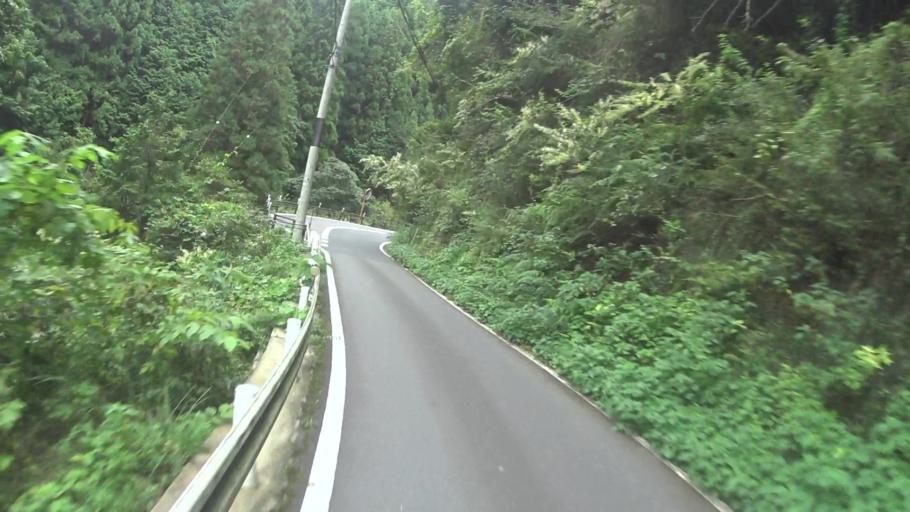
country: JP
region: Kyoto
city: Tanabe
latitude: 34.8040
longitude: 135.8483
